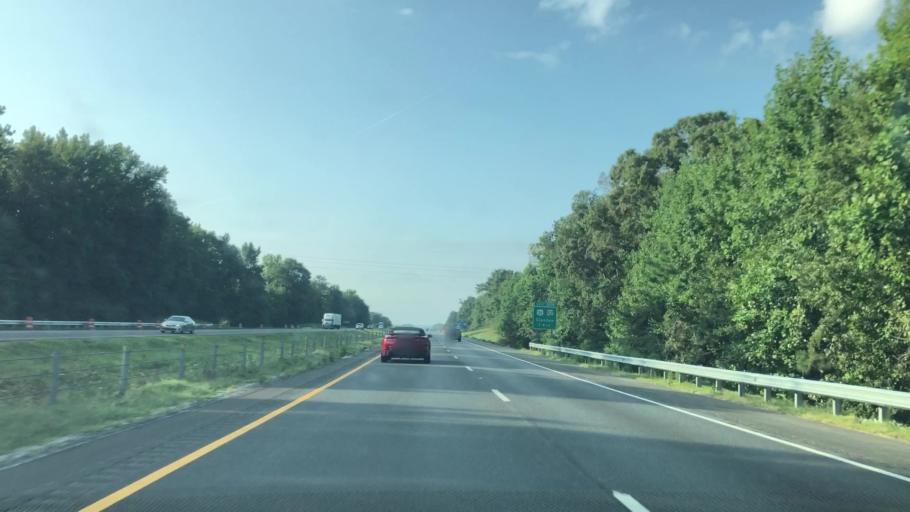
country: US
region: Alabama
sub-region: Chilton County
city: Clanton
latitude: 32.8176
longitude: -86.5861
